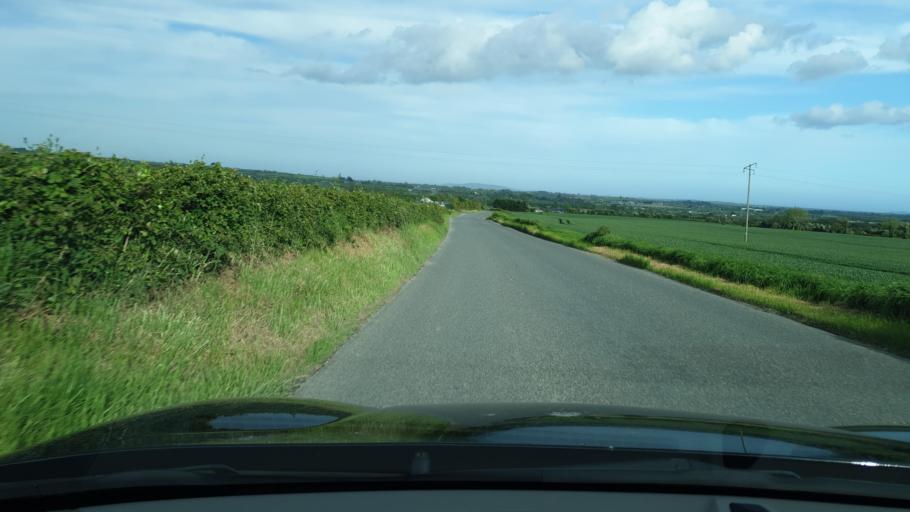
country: IE
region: Leinster
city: Balrothery
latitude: 53.5516
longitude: -6.2342
